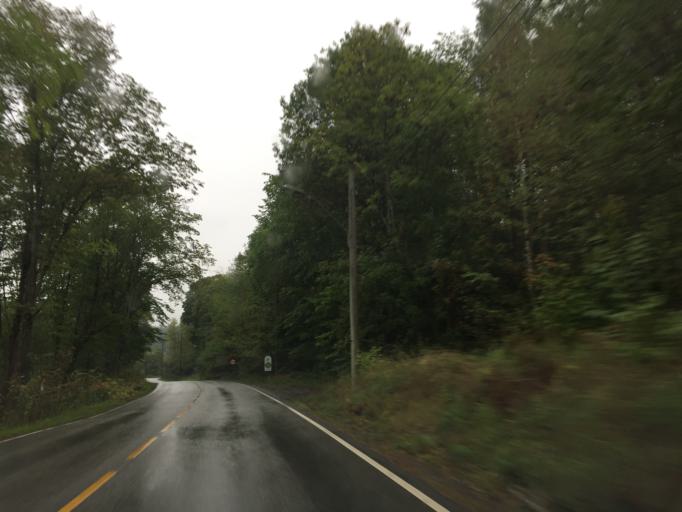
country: NO
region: Akershus
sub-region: Baerum
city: Lysaker
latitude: 59.9654
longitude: 10.6386
